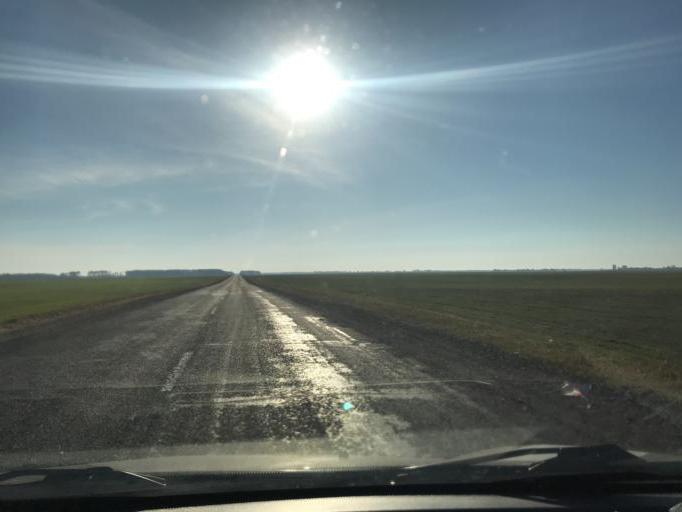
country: BY
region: Gomel
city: Khoyniki
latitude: 51.8304
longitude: 30.0585
